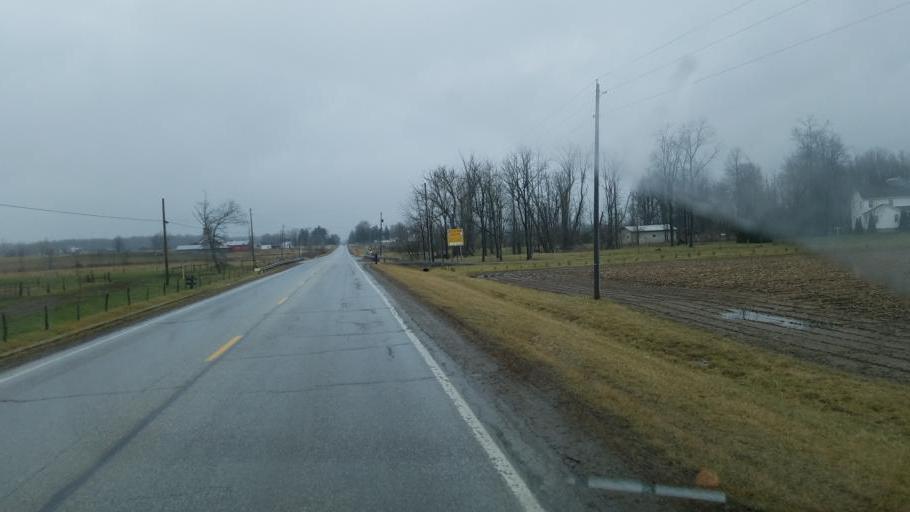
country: US
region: Ohio
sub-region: Geauga County
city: Middlefield
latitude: 41.4358
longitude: -80.9553
